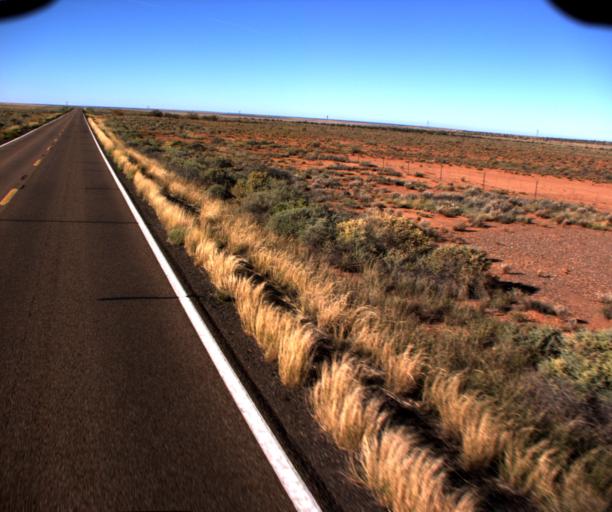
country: US
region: Arizona
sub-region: Navajo County
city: Holbrook
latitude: 34.8195
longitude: -110.1963
